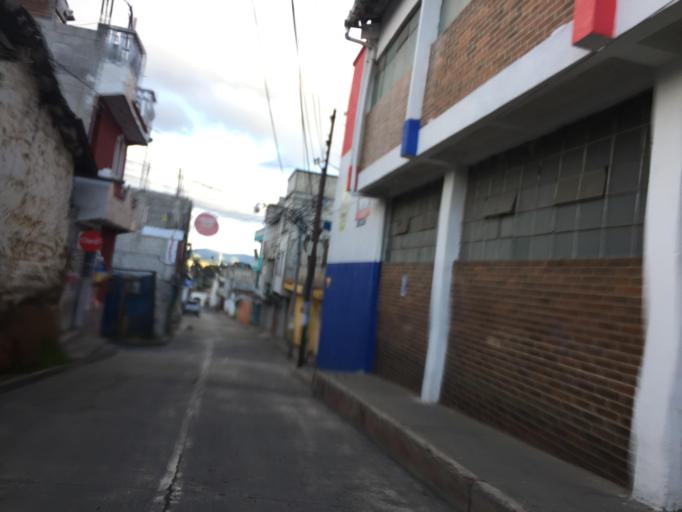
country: GT
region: Totonicapan
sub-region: Municipio de Totonicapan
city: Totonicapan
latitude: 14.9128
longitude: -91.3633
